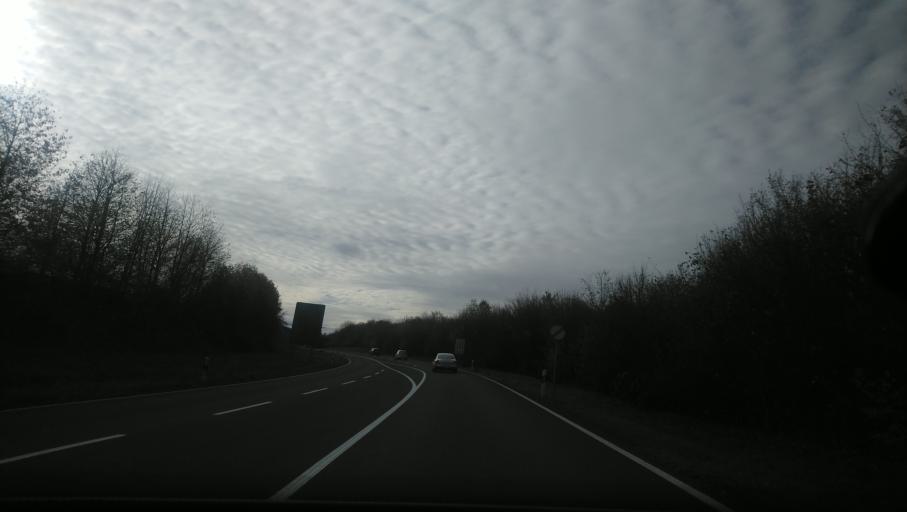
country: DE
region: Saxony
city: Zwonitz
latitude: 50.6396
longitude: 12.8217
